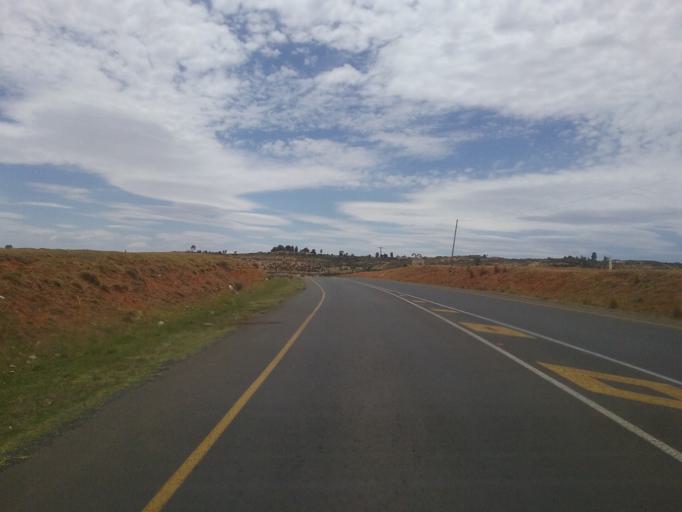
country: LS
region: Maseru
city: Maseru
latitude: -29.5062
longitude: 27.5271
